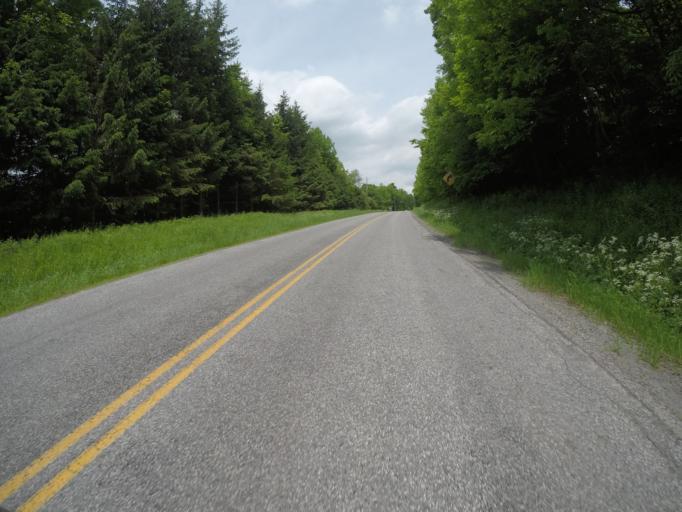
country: US
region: New York
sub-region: Delaware County
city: Stamford
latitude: 42.1775
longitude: -74.6738
